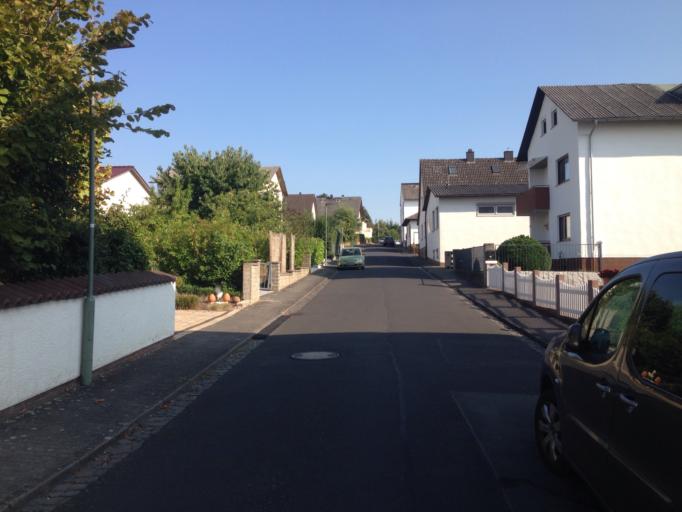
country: DE
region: Hesse
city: Allendorf an der Lahn
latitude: 50.5553
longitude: 8.6193
